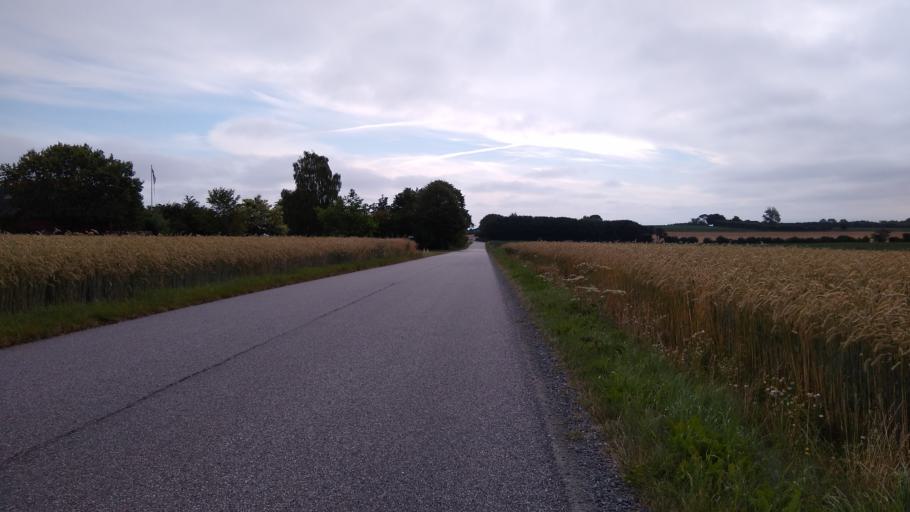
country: DK
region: South Denmark
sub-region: Vejle Kommune
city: Brejning
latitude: 55.6482
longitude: 9.7172
